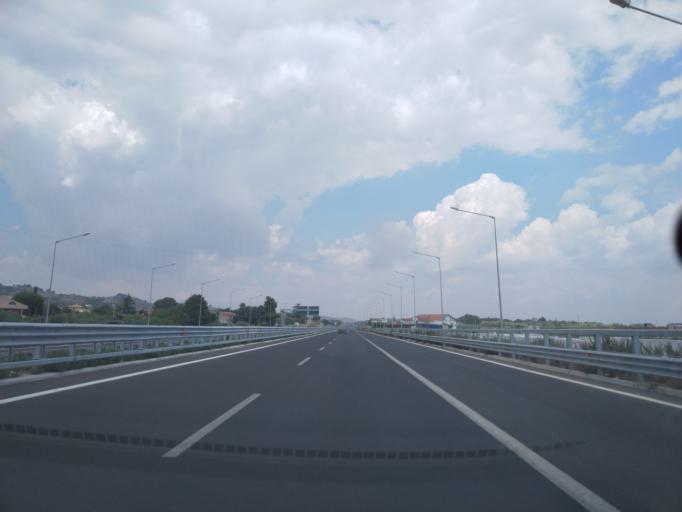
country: IT
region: Sicily
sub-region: Agrigento
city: Racalmuto
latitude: 37.3756
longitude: 13.7203
